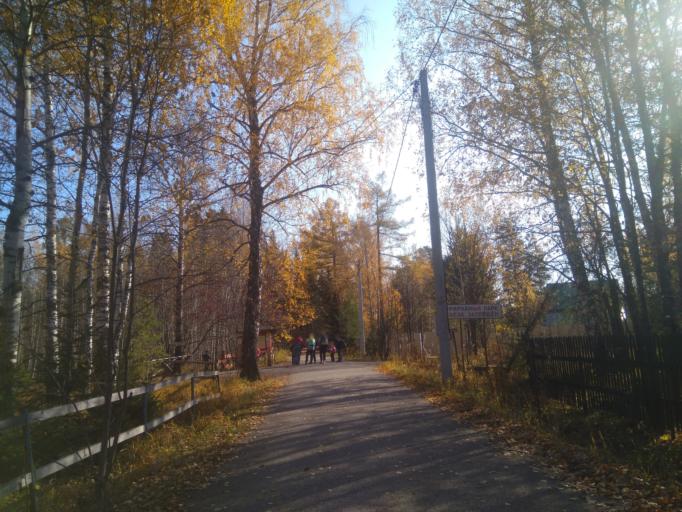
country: RU
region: Sverdlovsk
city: Mikhaylovsk
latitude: 56.5232
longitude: 59.2333
